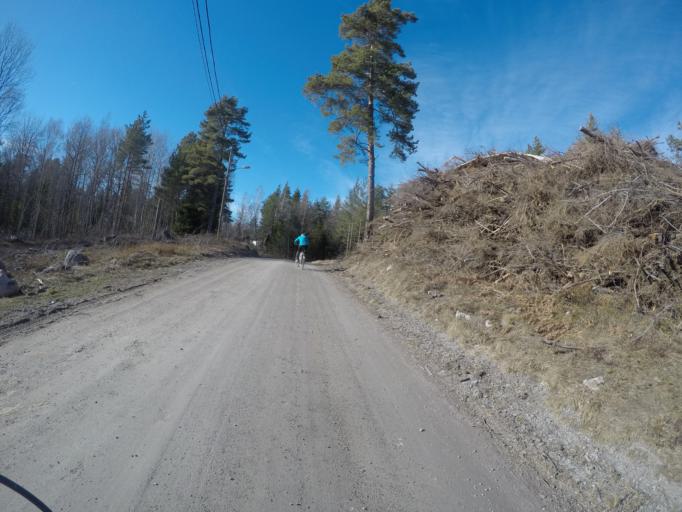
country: SE
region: Soedermanland
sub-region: Eskilstuna Kommun
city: Torshalla
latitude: 59.4248
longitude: 16.4461
